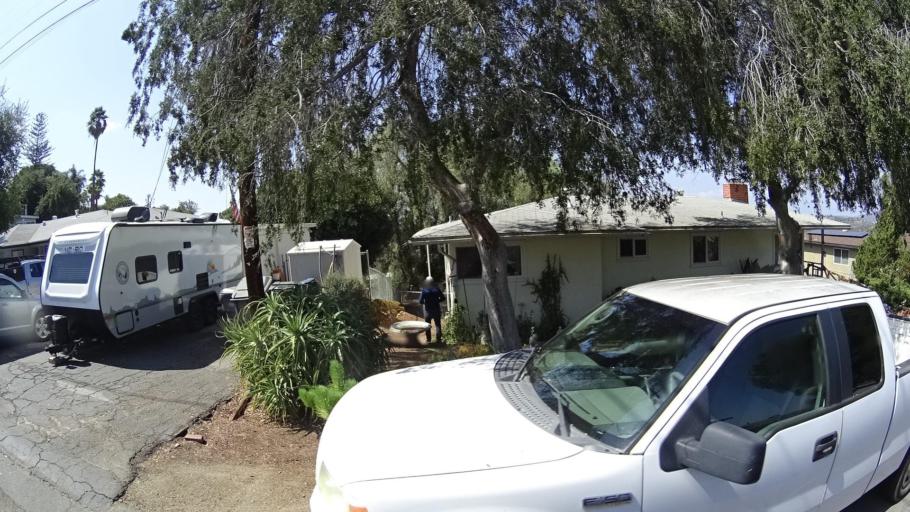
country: US
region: California
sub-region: San Diego County
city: Spring Valley
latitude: 32.7383
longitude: -116.9845
